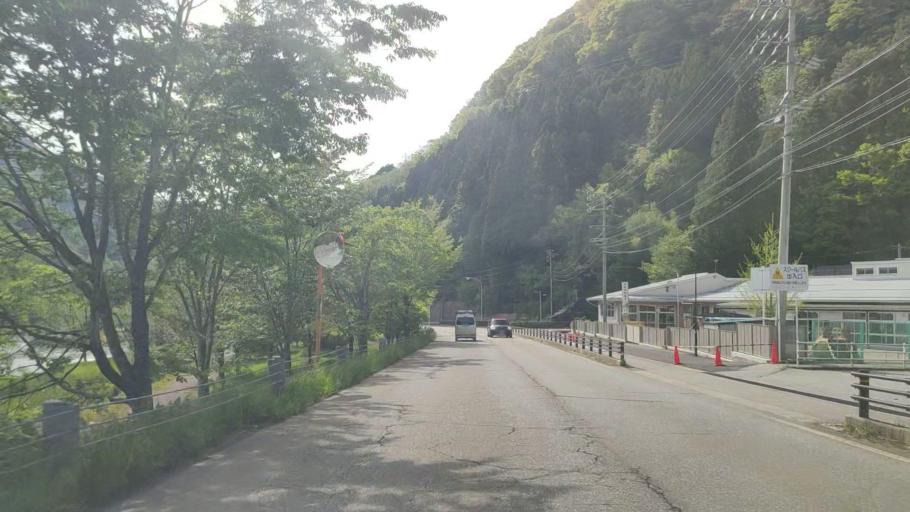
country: JP
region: Gifu
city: Takayama
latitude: 36.2484
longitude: 137.5135
